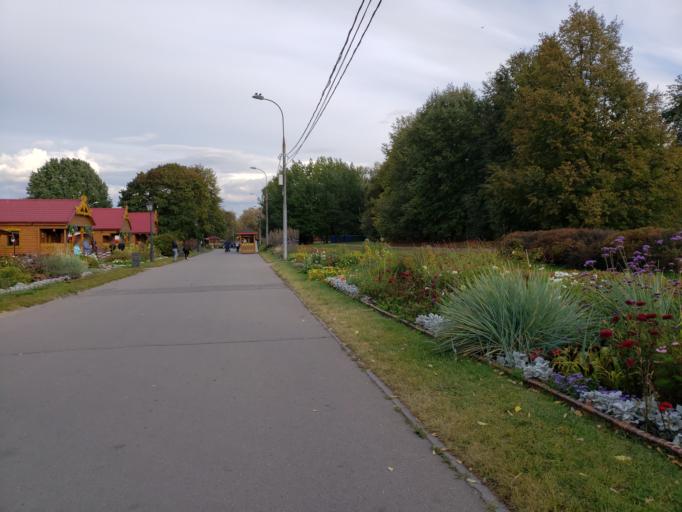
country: RU
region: Moscow
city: Kolomenskoye
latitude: 55.6711
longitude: 37.6691
